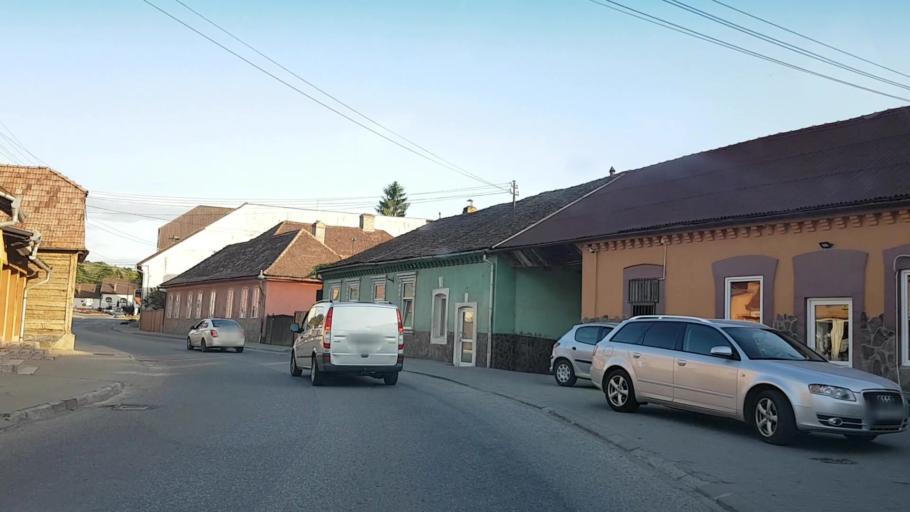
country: RO
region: Harghita
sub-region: Comuna Praid
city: Praid
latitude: 46.5523
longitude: 25.1263
